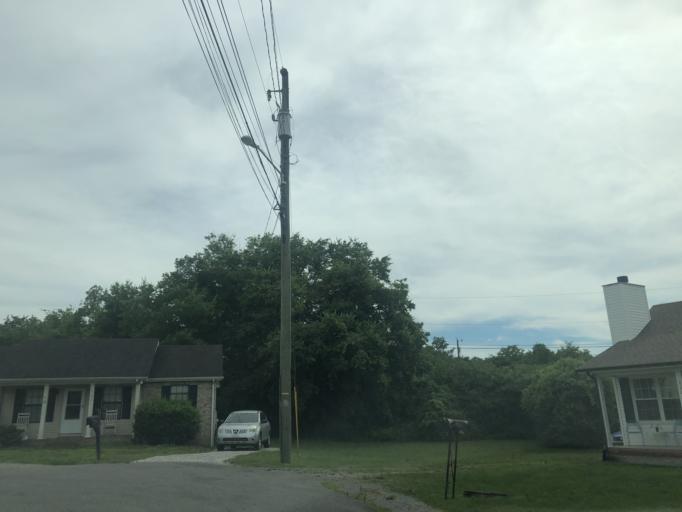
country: US
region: Tennessee
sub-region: Davidson County
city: Nashville
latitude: 36.2090
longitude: -86.8202
